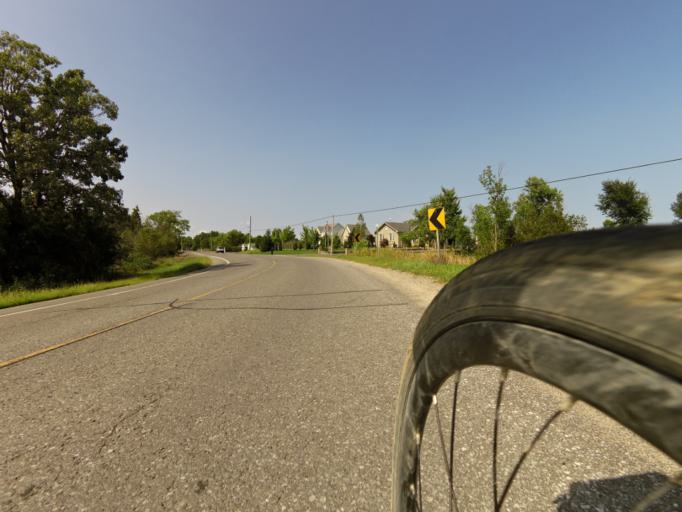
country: CA
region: Ontario
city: Skatepark
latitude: 44.2489
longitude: -76.7204
